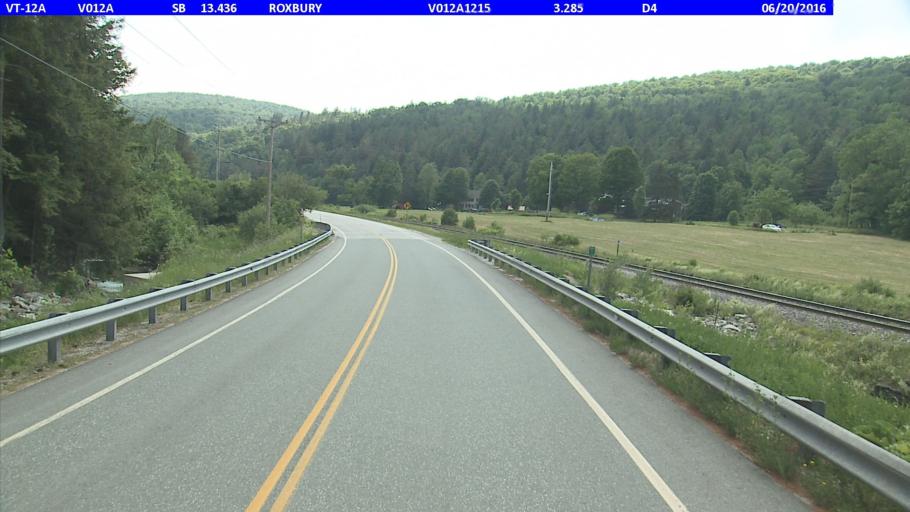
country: US
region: Vermont
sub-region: Washington County
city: Northfield
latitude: 44.0751
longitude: -72.7434
